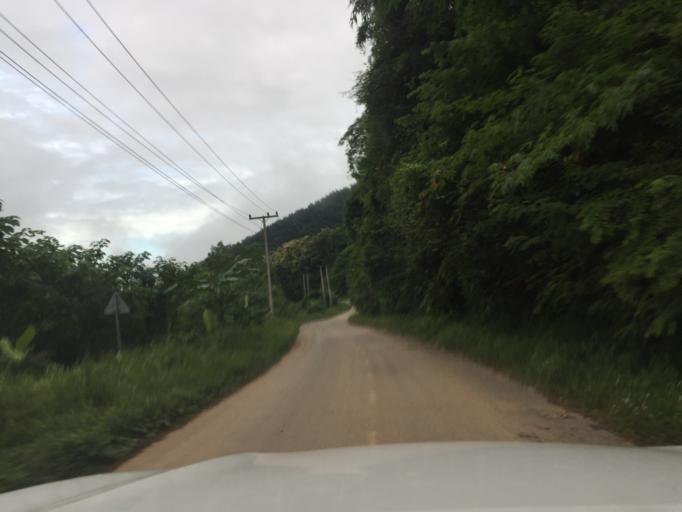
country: LA
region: Phongsali
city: Khoa
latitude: 21.0790
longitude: 102.3750
